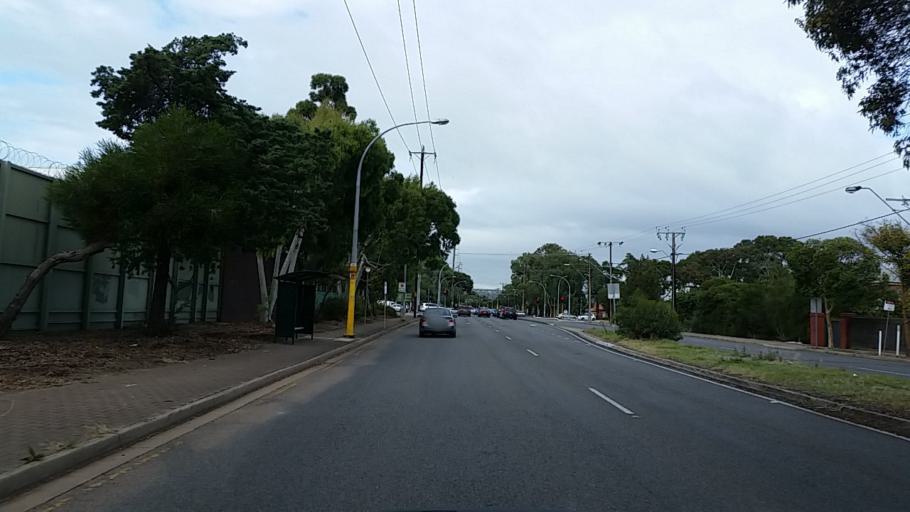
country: AU
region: South Australia
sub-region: Marion
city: Plympton Park
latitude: -34.9947
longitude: 138.5393
